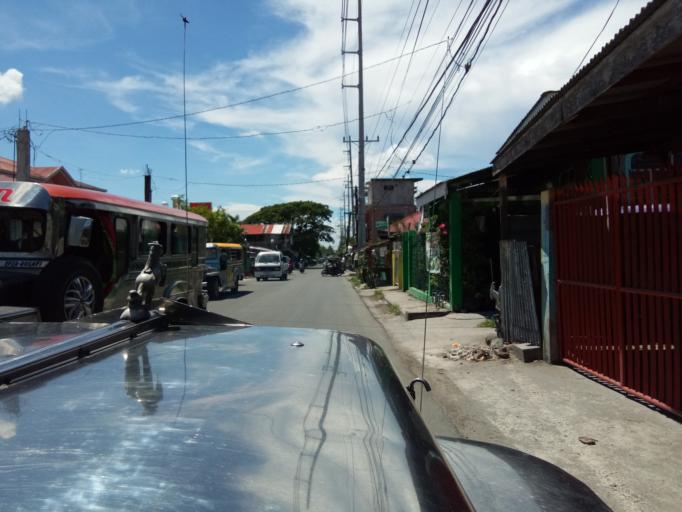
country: PH
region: Calabarzon
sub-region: Province of Cavite
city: Pasong Kawayan Primero
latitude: 14.3576
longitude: 120.8982
